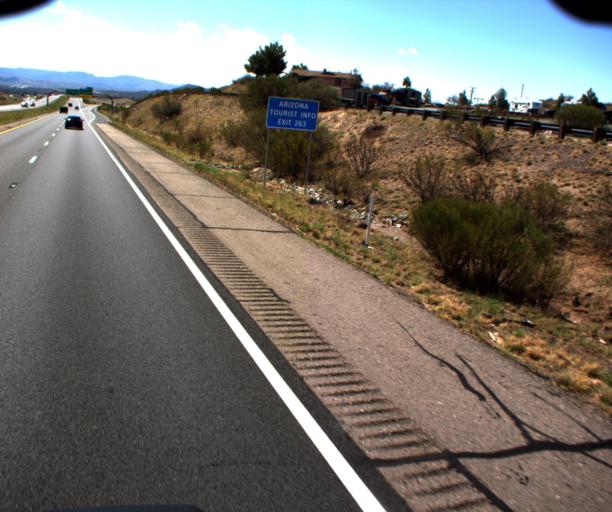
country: US
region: Arizona
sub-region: Yavapai County
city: Spring Valley
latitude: 34.3376
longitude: -112.1324
